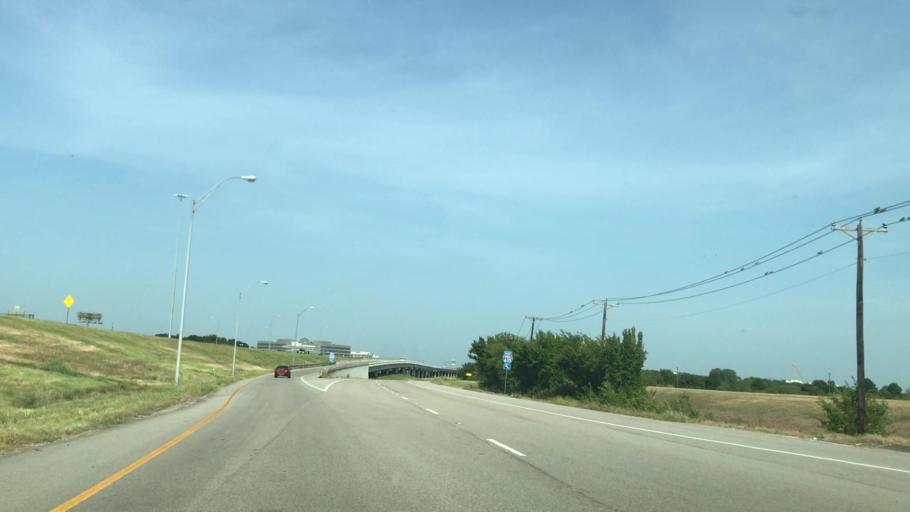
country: US
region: Texas
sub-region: Dallas County
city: Farmers Branch
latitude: 32.9100
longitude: -96.9399
